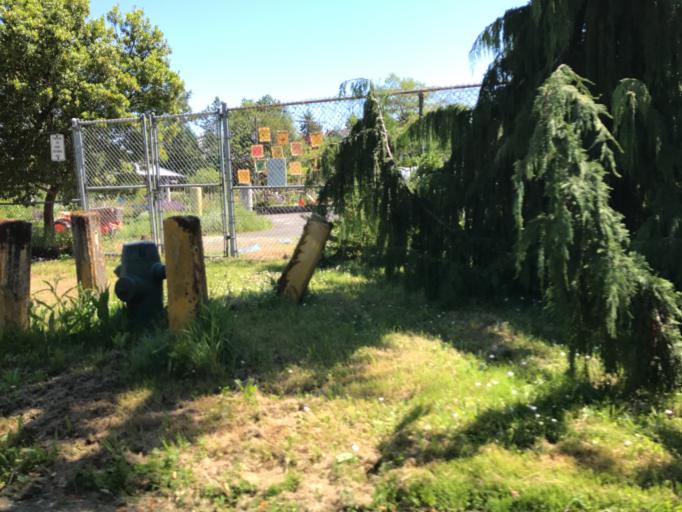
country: US
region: Washington
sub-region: King County
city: Seattle
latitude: 47.5871
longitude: -122.2960
